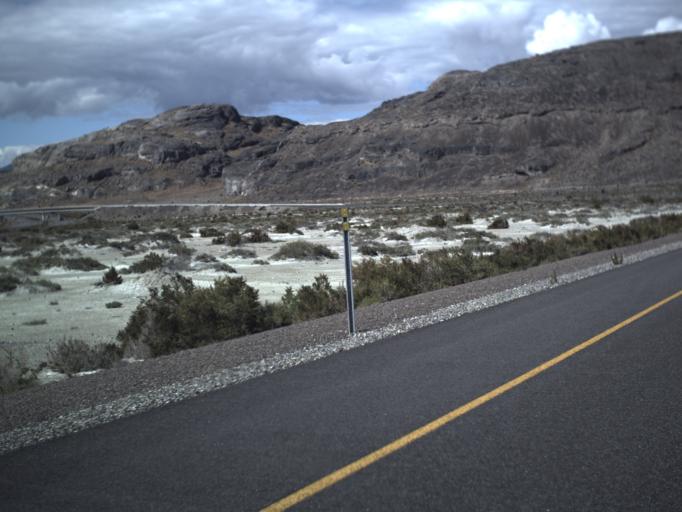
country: US
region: Utah
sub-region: Tooele County
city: Wendover
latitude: 40.7479
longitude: -114.0068
